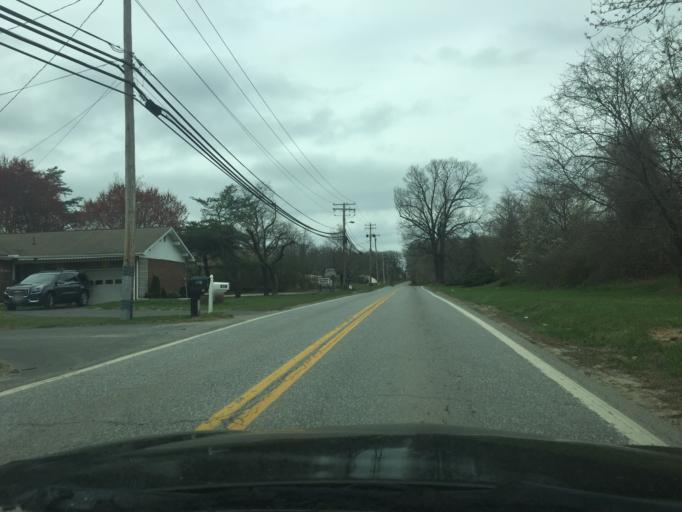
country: US
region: Maryland
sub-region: Baltimore County
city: Bowleys Quarters
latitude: 39.3571
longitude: -76.3939
